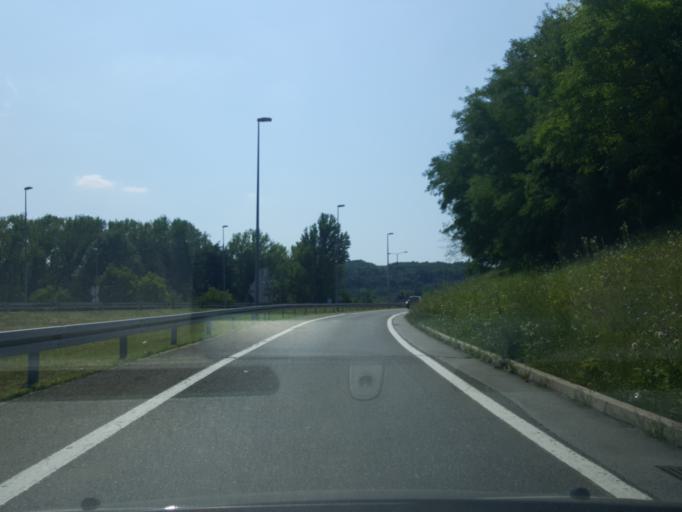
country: RS
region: Central Serbia
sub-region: Belgrade
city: Sopot
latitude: 44.5651
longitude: 20.6684
